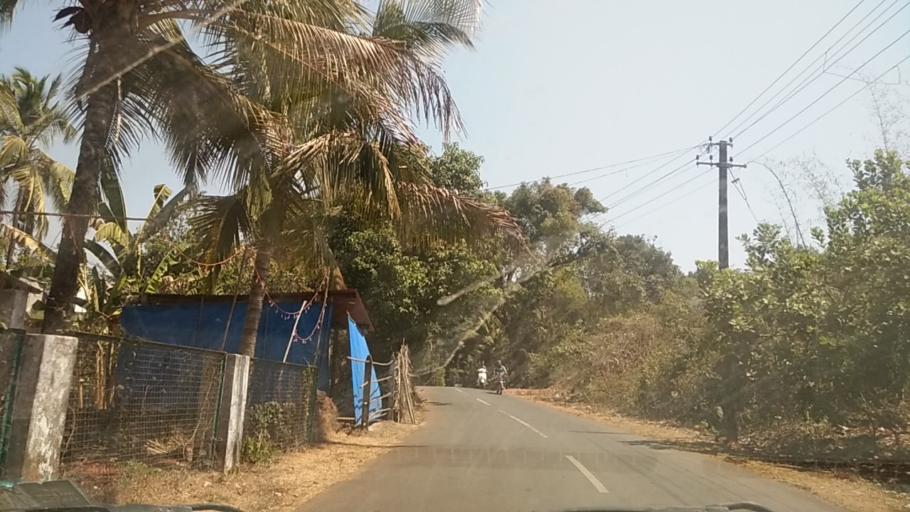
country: IN
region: Goa
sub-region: North Goa
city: Dicholi
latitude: 15.5753
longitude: 73.9130
